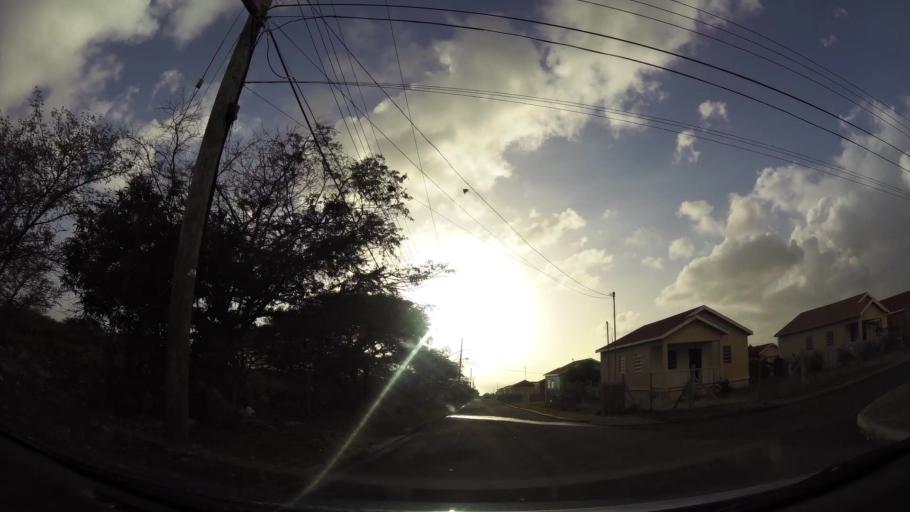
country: KN
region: Saint John Figtree
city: Fig Tree
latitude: 17.1173
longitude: -62.6133
